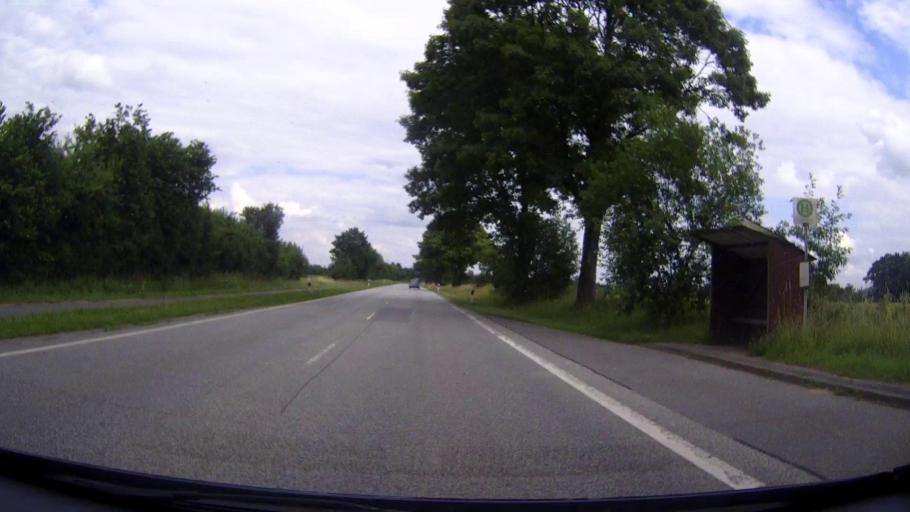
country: DE
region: Schleswig-Holstein
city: Aukrug
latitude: 54.0699
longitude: 9.8127
